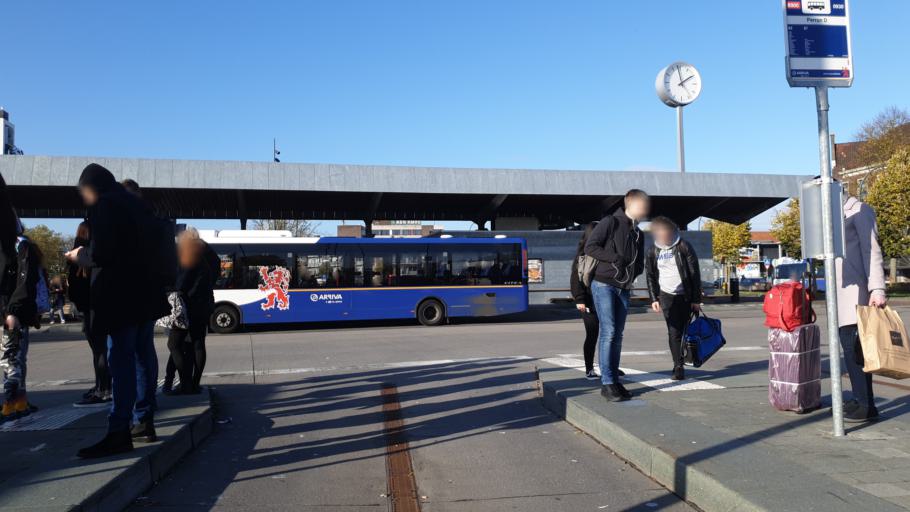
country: NL
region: Limburg
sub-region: Gemeente Venlo
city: Venlo
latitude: 51.3648
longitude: 6.1726
